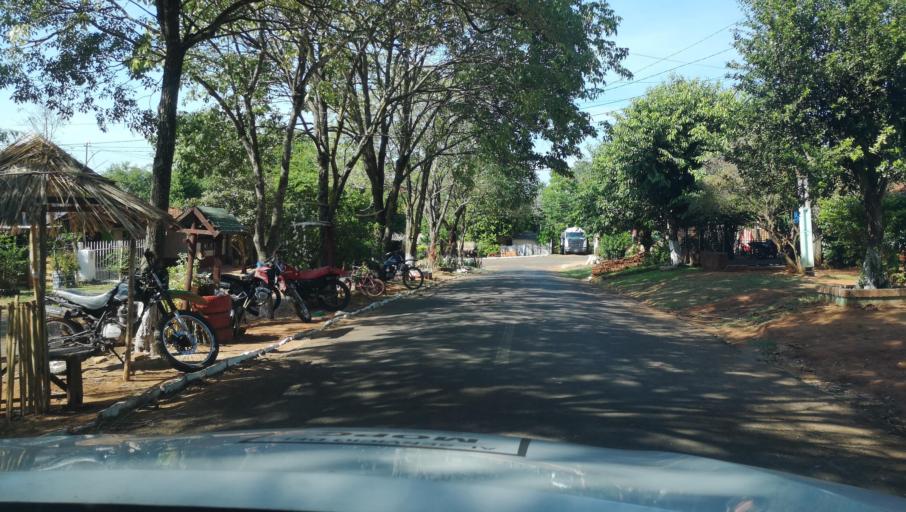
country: PY
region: Misiones
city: Santa Maria
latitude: -26.8937
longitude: -57.0197
